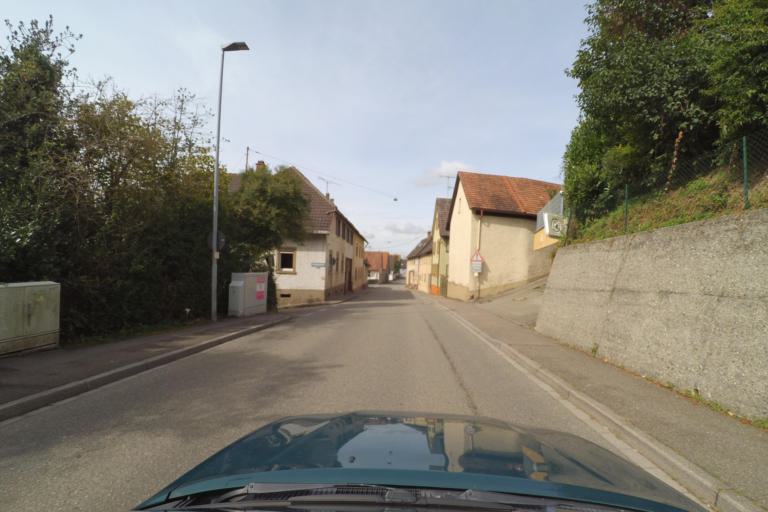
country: DE
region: Baden-Wuerttemberg
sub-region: Freiburg Region
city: Kippenheim
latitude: 48.2913
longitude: 7.8289
